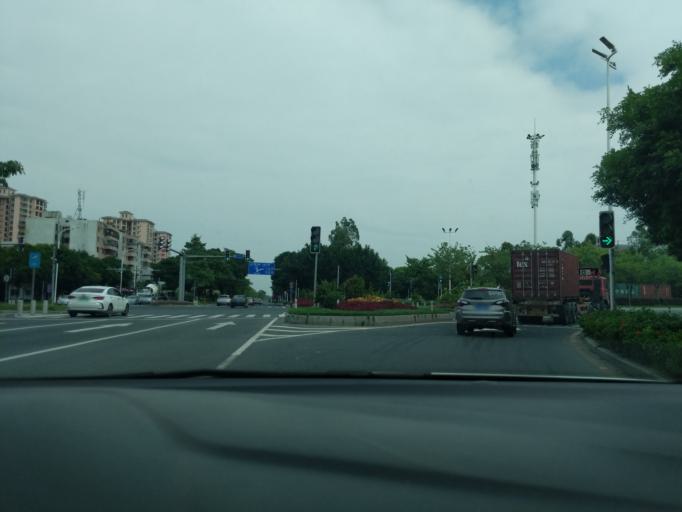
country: CN
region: Guangdong
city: Nansha
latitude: 22.7509
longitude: 113.5807
